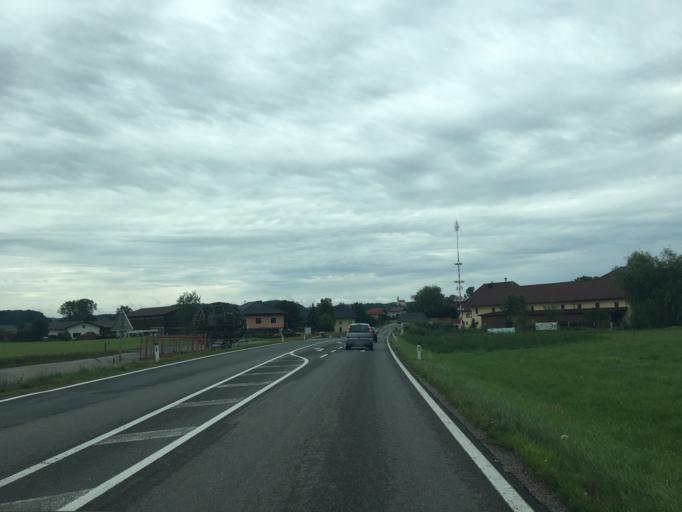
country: AT
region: Salzburg
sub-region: Politischer Bezirk Salzburg-Umgebung
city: Dorfbeuern
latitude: 48.0290
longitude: 12.9729
